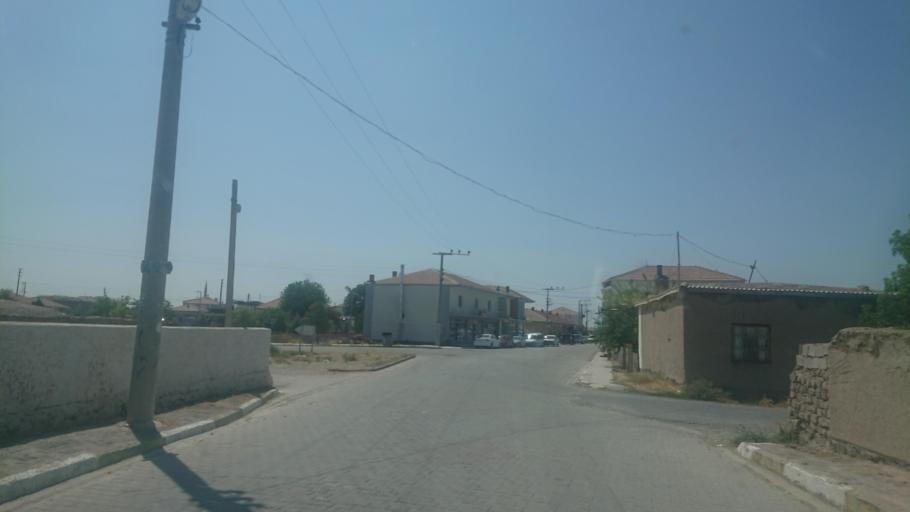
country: TR
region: Aksaray
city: Yesilova
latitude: 38.3447
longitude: 33.7510
